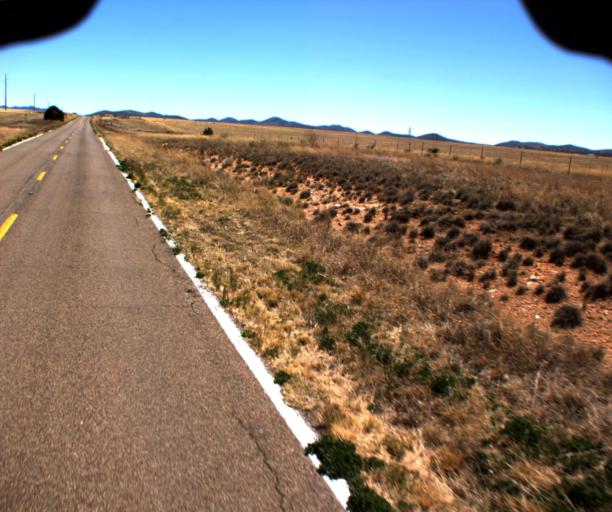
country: US
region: Arizona
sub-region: Cochise County
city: Huachuca City
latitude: 31.6334
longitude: -110.5965
